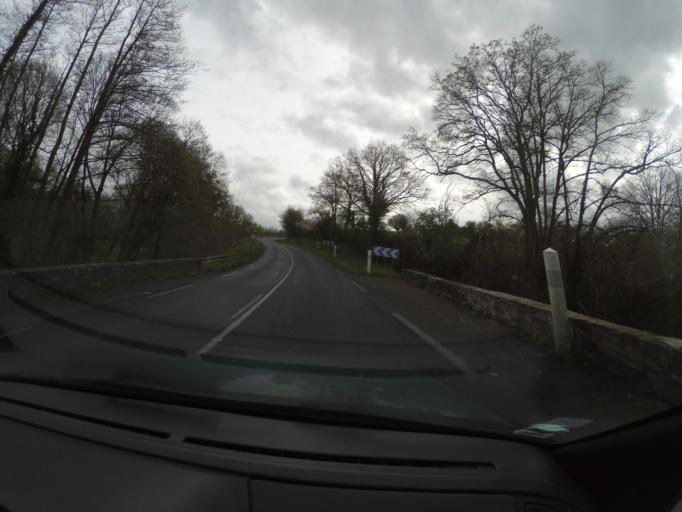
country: FR
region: Pays de la Loire
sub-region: Departement de Maine-et-Loire
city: Saint-Laurent-des-Autels
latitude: 47.3024
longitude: -1.1651
